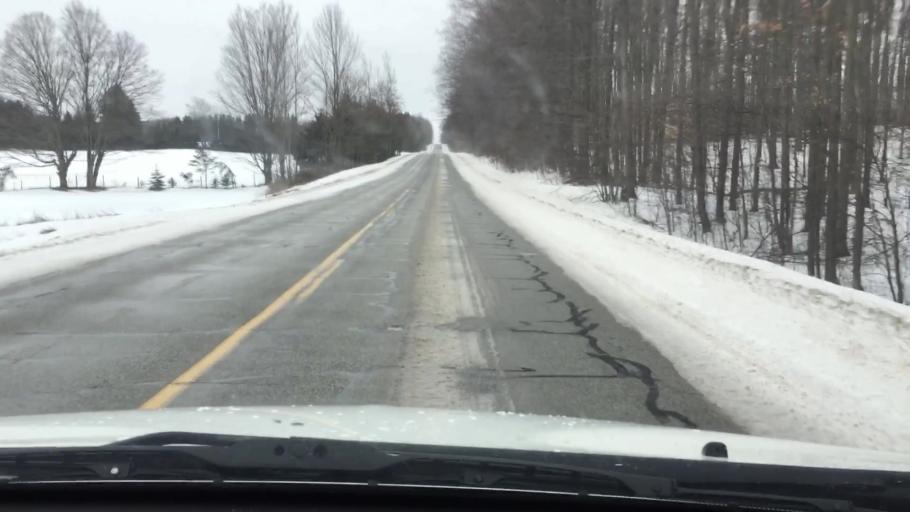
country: US
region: Michigan
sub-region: Wexford County
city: Cadillac
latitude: 44.1913
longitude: -85.4057
